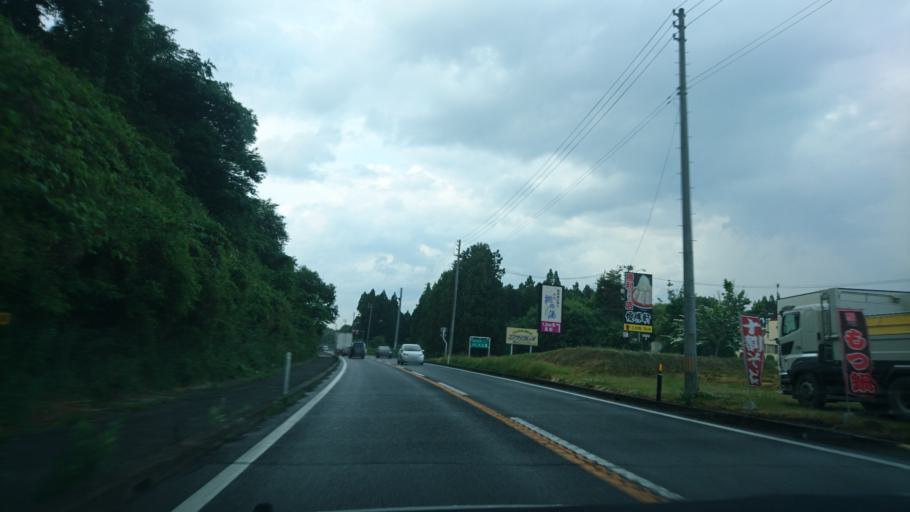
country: JP
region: Iwate
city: Ichinoseki
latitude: 38.9521
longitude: 141.1212
